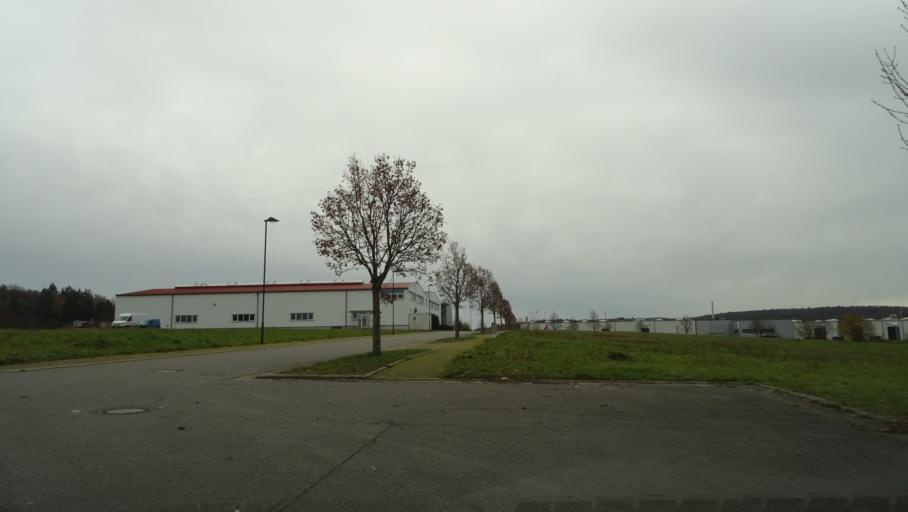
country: DE
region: Baden-Wuerttemberg
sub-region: Karlsruhe Region
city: Binau
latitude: 49.3460
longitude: 9.0413
